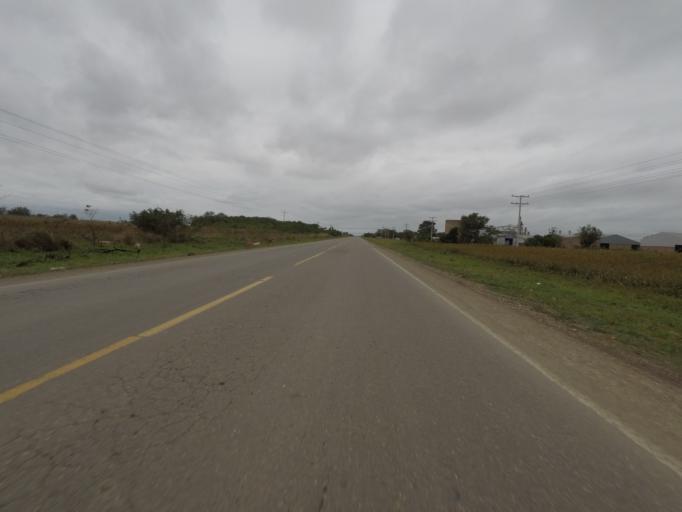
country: BO
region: Santa Cruz
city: Okinawa Numero Uno
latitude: -17.2454
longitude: -62.5554
